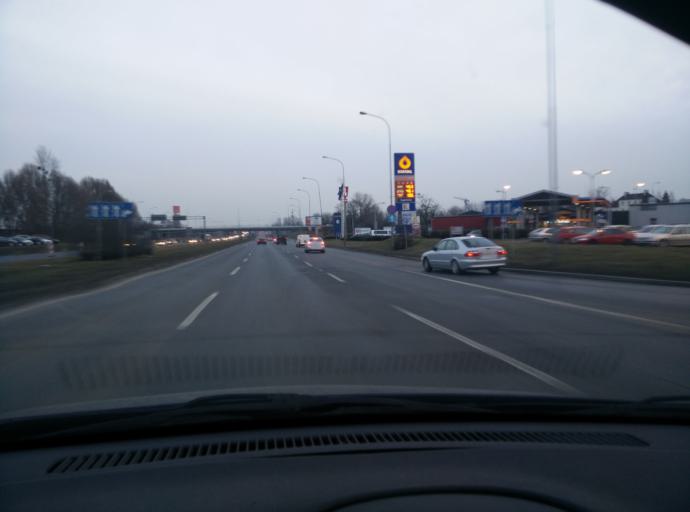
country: PL
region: Greater Poland Voivodeship
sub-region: Poznan
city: Poznan
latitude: 52.3833
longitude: 16.9734
